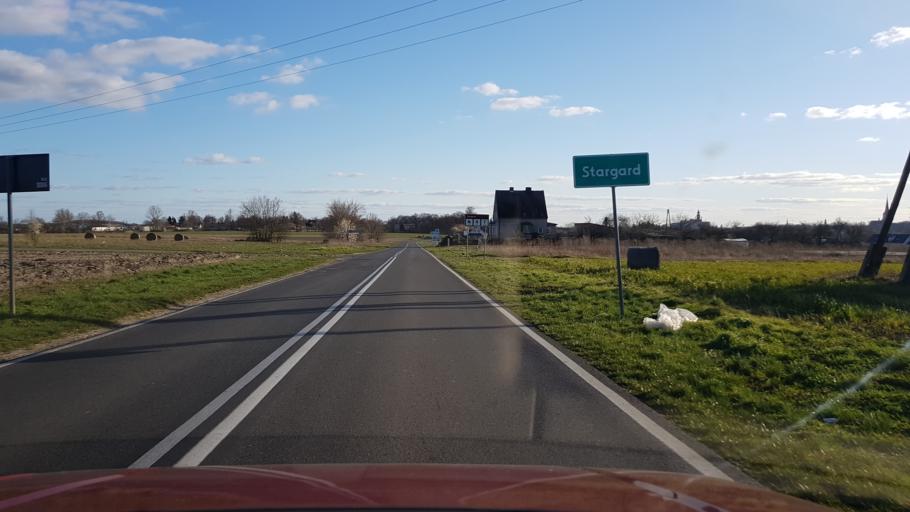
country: PL
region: West Pomeranian Voivodeship
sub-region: Powiat stargardzki
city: Stargard Szczecinski
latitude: 53.3545
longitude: 15.0609
